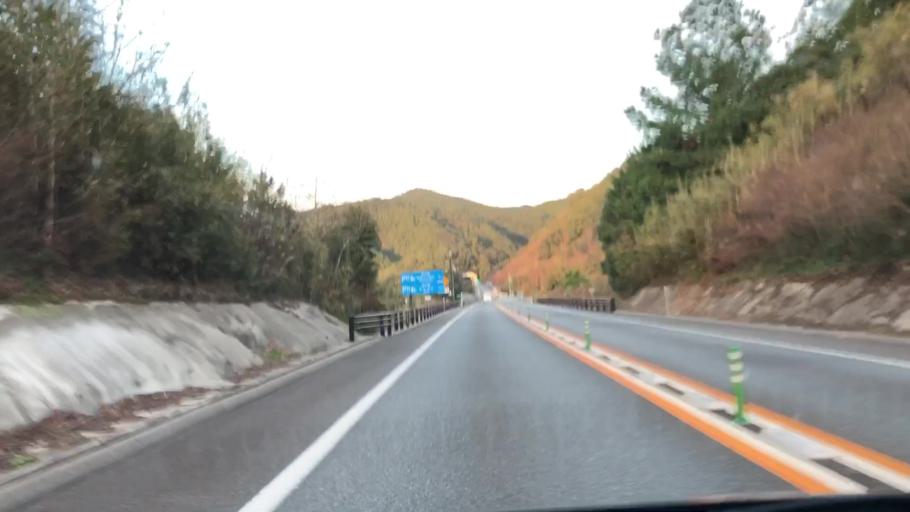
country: JP
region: Kumamoto
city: Minamata
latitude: 32.2776
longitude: 130.4967
